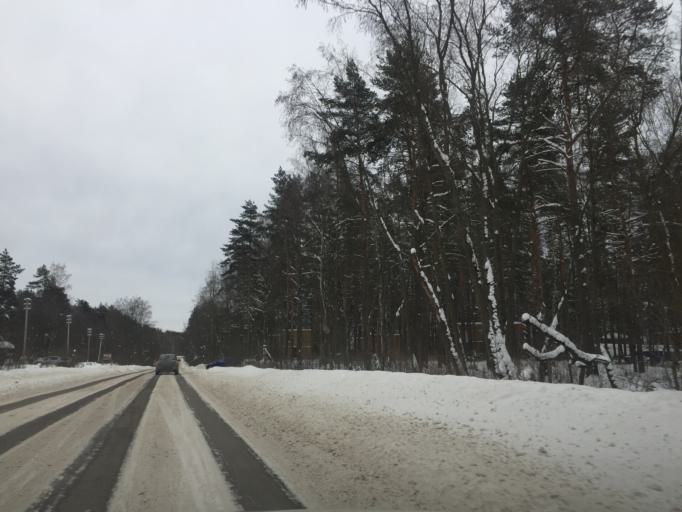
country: RU
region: Leningrad
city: Imeni Sverdlova
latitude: 59.7875
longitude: 30.7269
